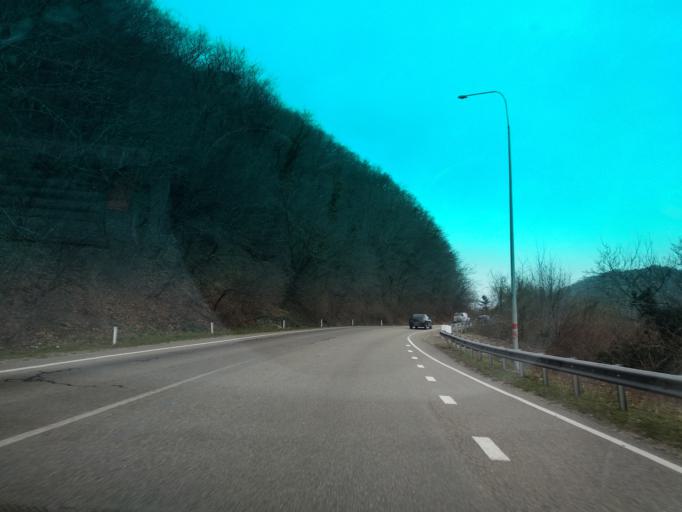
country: RU
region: Krasnodarskiy
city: Ol'ginka
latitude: 44.2199
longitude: 38.8944
